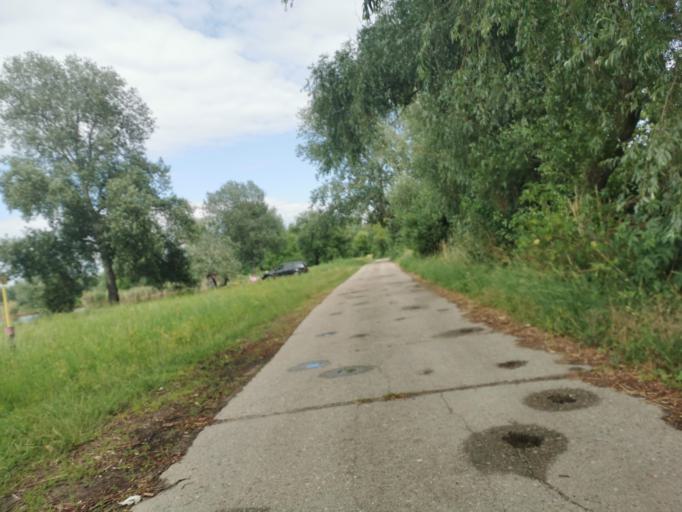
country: CZ
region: South Moravian
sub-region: Okres Hodonin
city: Mikulcice
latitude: 48.7628
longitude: 17.0702
